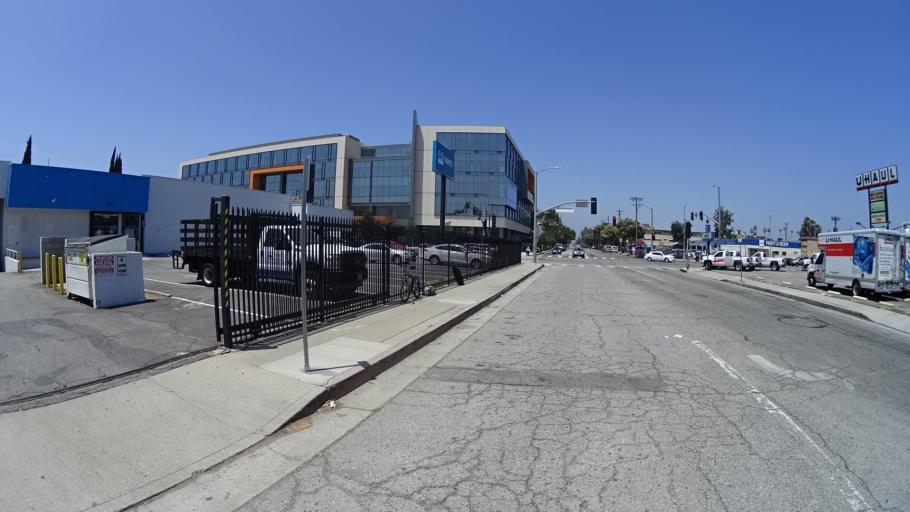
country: US
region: California
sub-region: Los Angeles County
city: Van Nuys
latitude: 34.2085
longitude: -118.4482
